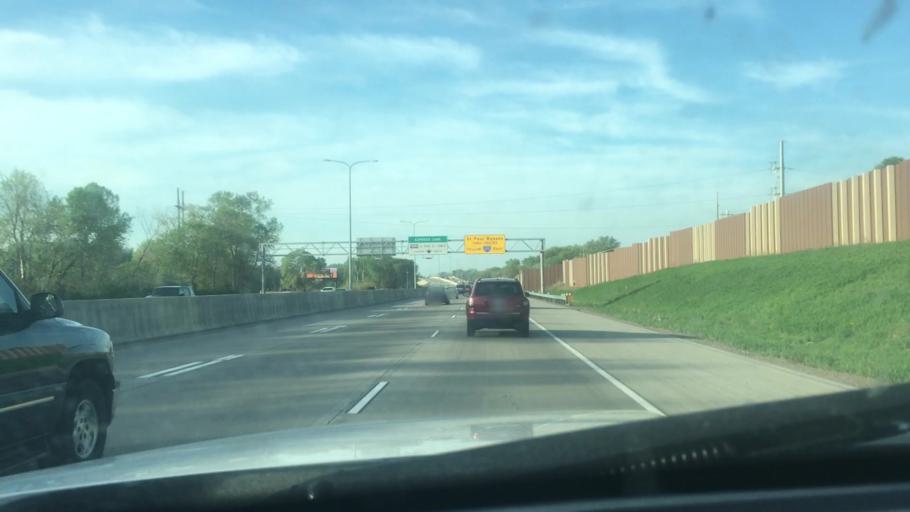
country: US
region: Minnesota
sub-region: Ramsey County
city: Vadnais Heights
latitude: 45.0665
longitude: -93.0551
